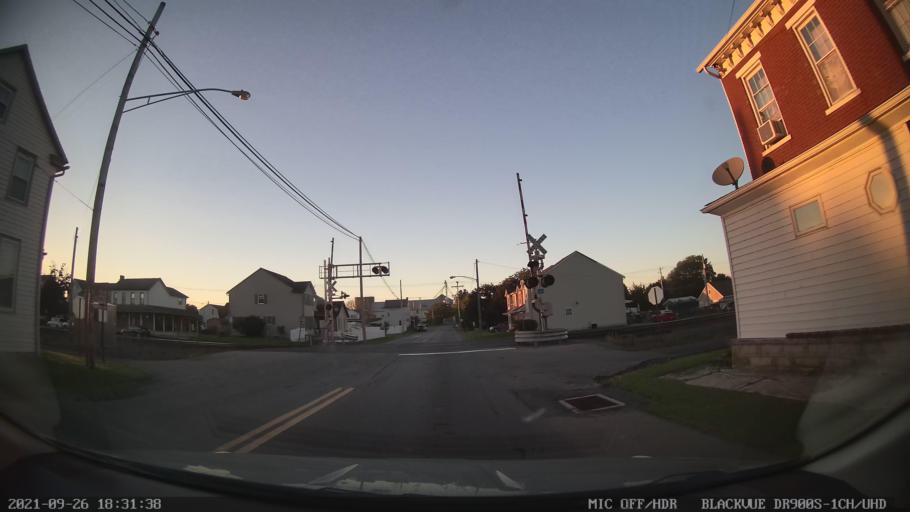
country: US
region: Pennsylvania
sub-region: Berks County
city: Kutztown
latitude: 40.4819
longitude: -75.7574
